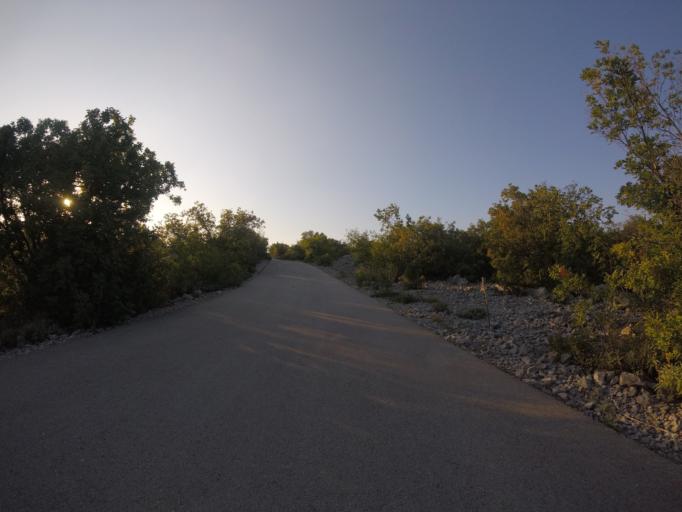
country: HR
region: Primorsko-Goranska
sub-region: Grad Crikvenica
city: Jadranovo
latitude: 45.2076
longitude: 14.6450
